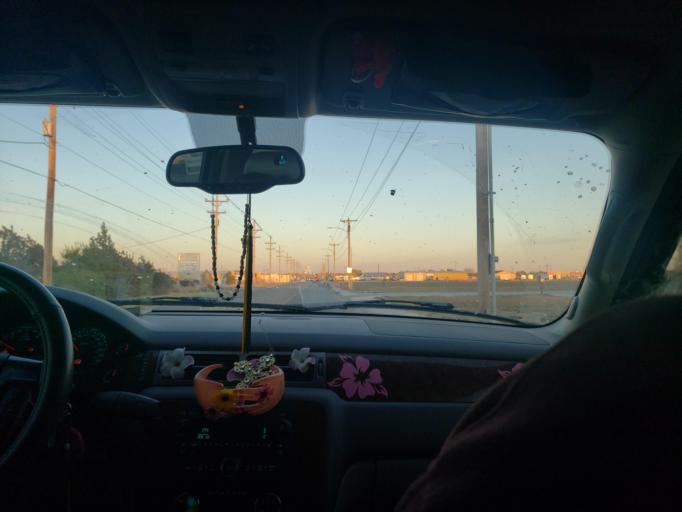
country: US
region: Kansas
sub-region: Finney County
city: Garden City
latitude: 37.9895
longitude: -100.8883
